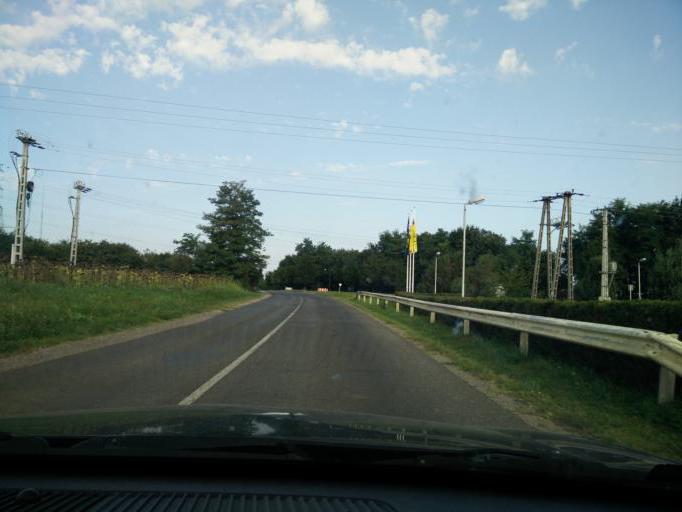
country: HU
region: Tolna
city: Bonyhad
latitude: 46.2987
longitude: 18.5071
